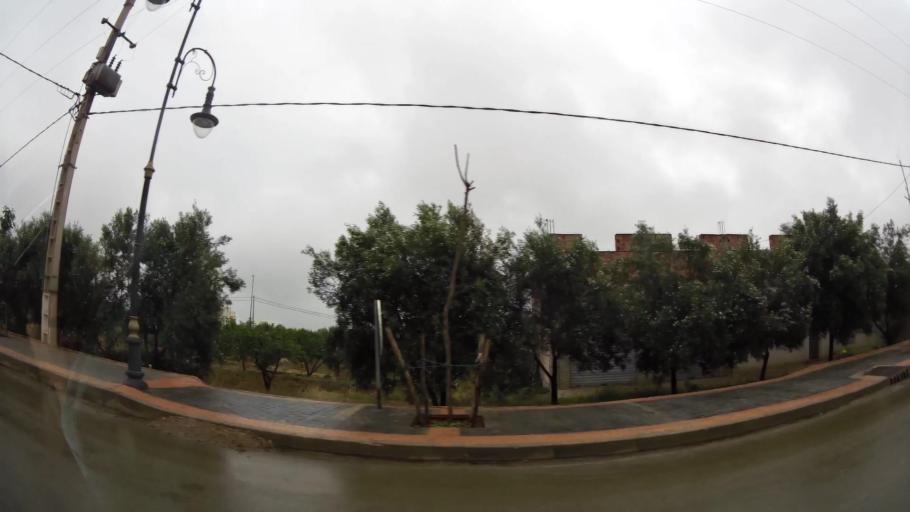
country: MA
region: Taza-Al Hoceima-Taounate
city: Imzourene
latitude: 35.1710
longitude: -3.8616
